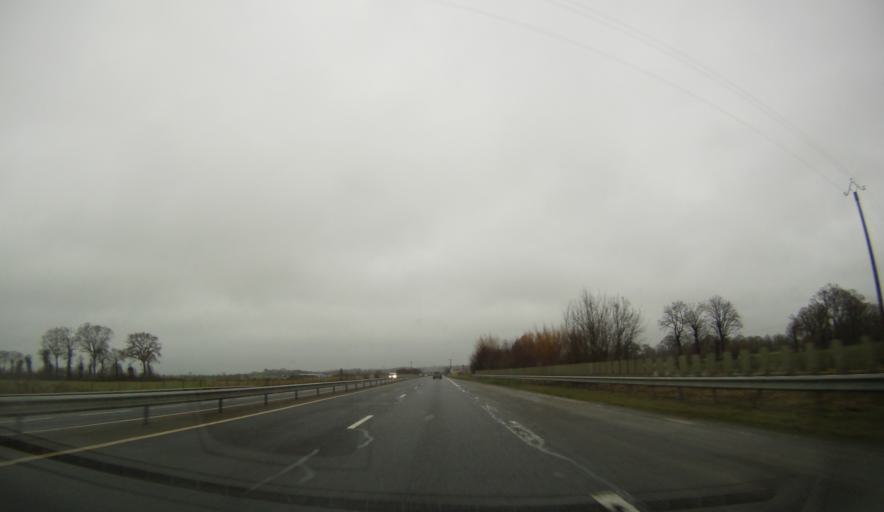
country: FR
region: Brittany
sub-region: Departement d'Ille-et-Vilaine
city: Saint-Armel
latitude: 48.0187
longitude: -1.6016
